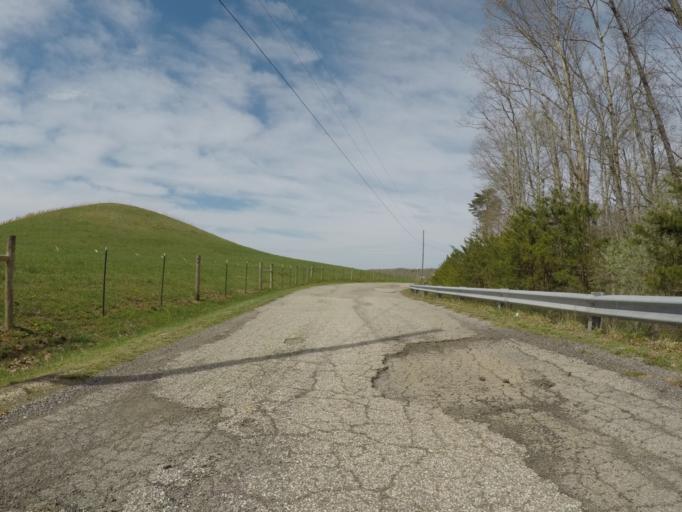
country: US
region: West Virginia
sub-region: Wayne County
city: Lavalette
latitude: 38.3289
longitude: -82.3575
